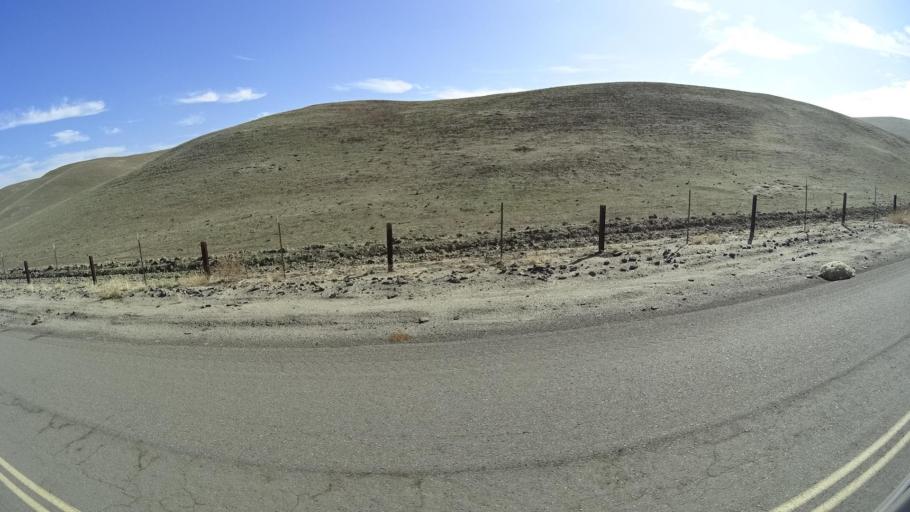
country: US
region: California
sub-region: Tulare County
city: Richgrove
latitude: 35.6362
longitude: -118.9494
